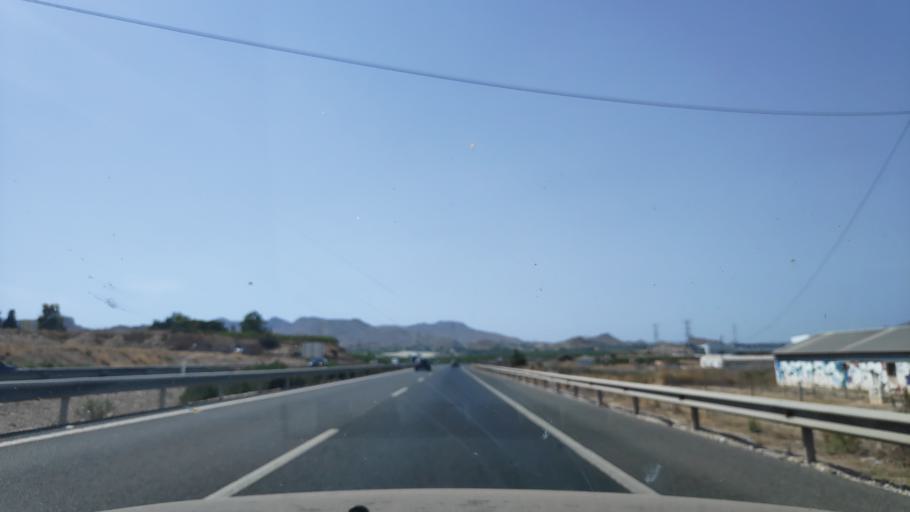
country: ES
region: Murcia
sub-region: Murcia
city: Archena
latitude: 38.1321
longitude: -1.2656
